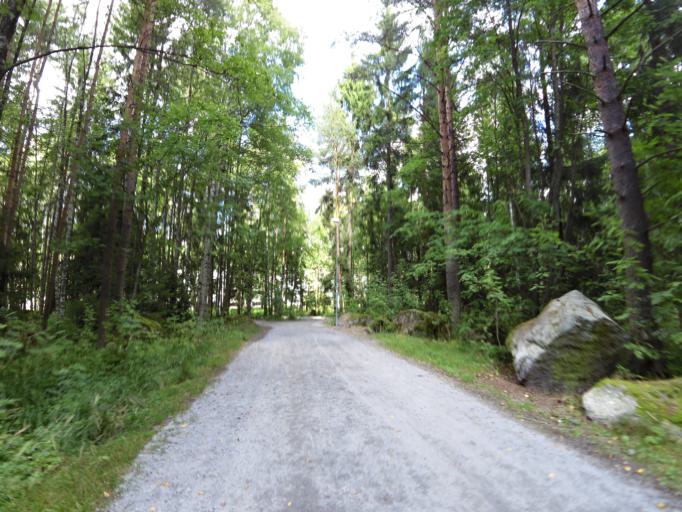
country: FI
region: Pirkanmaa
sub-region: Tampere
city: Yloejaervi
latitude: 61.5094
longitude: 23.6101
